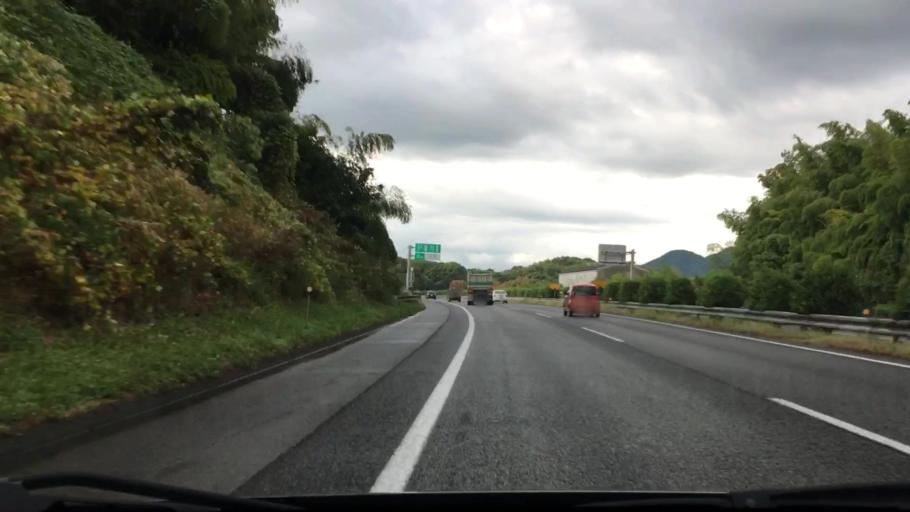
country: JP
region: Fukuoka
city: Koga
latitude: 33.7229
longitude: 130.4997
